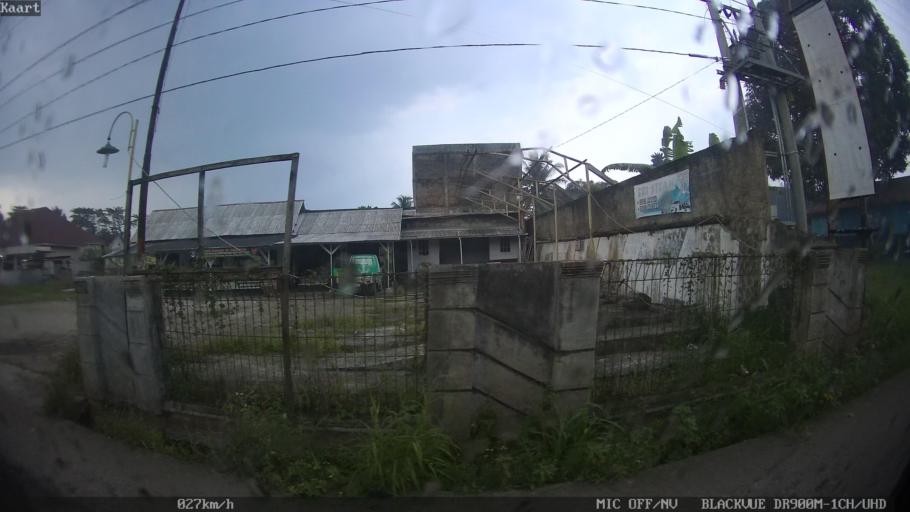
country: ID
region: Lampung
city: Gedongtataan
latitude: -5.3791
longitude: 105.1125
